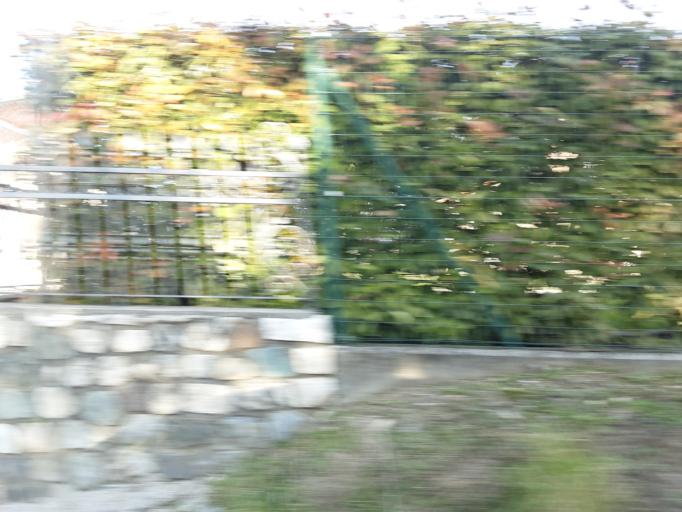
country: IT
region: Veneto
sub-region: Provincia di Treviso
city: Vittorio Veneto
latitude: 45.9683
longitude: 12.3008
